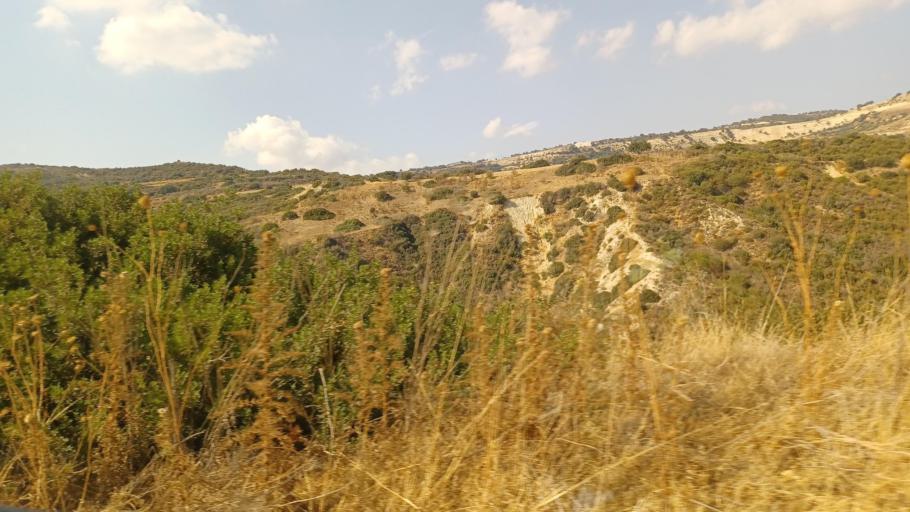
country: CY
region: Pafos
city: Polis
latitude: 34.9939
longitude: 32.4328
